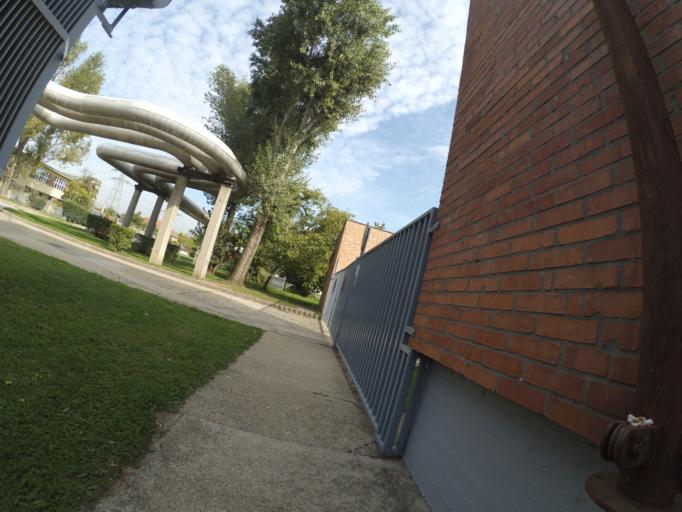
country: HU
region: Budapest
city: Budapest III. keruelet
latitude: 47.5628
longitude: 19.0361
